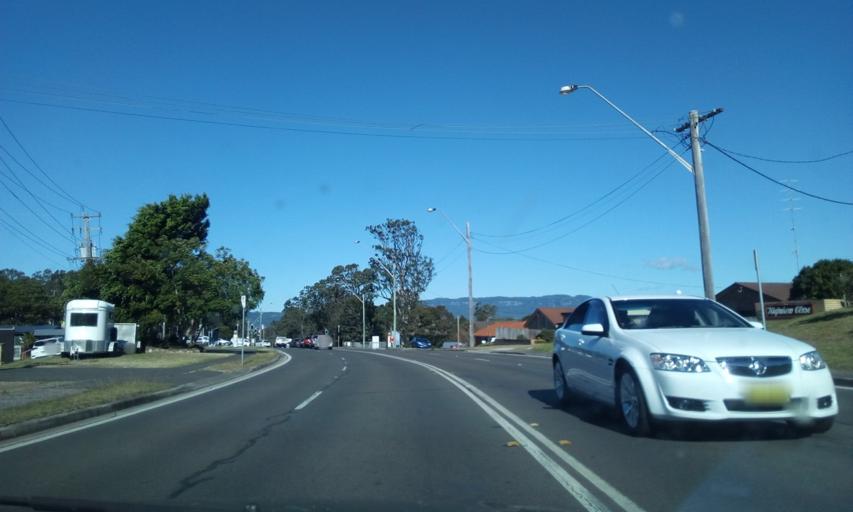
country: AU
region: New South Wales
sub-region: Wollongong
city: Dapto
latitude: -34.5117
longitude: 150.7849
